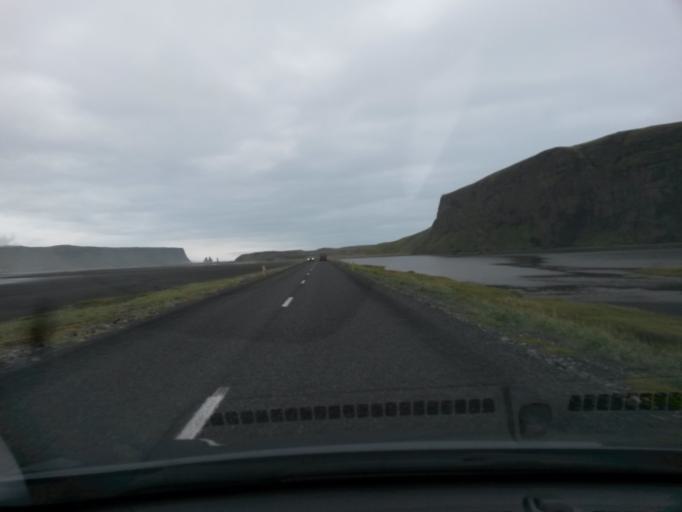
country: IS
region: South
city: Vestmannaeyjar
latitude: 63.4129
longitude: -19.1364
